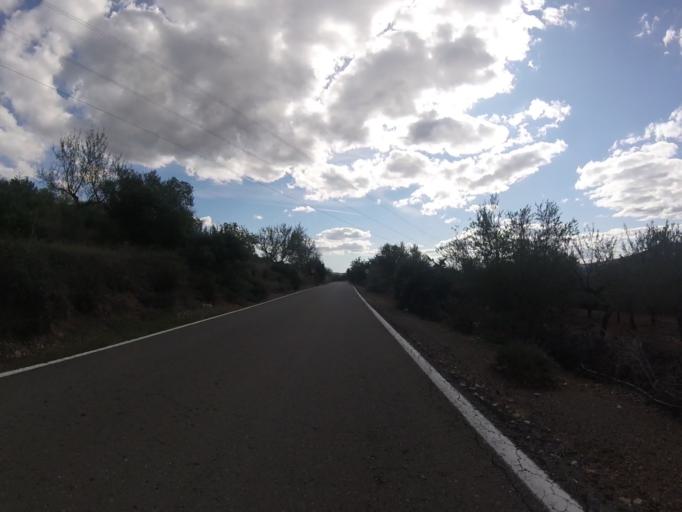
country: ES
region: Valencia
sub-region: Provincia de Castello
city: Cuevas de Vinroma
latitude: 40.3587
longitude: 0.1254
